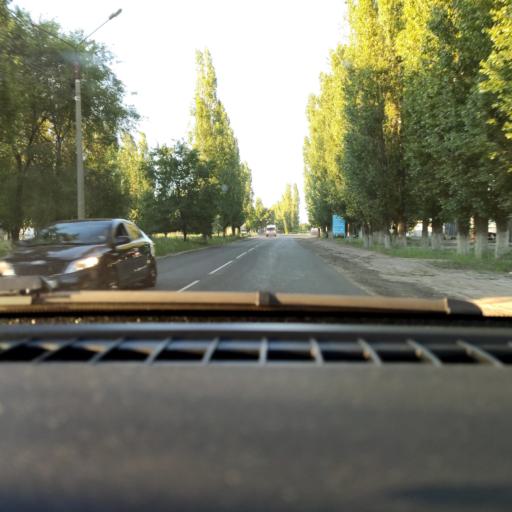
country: RU
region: Voronezj
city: Maslovka
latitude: 51.5835
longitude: 39.3184
